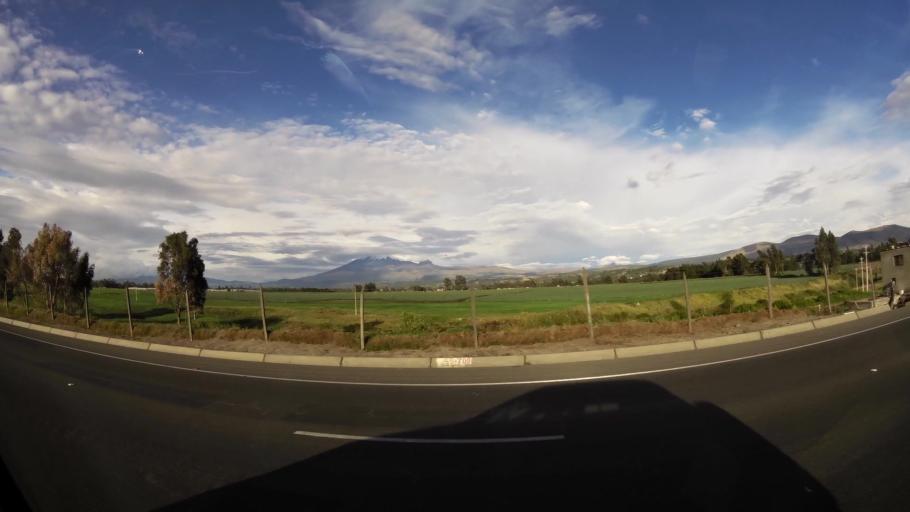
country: EC
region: Cotopaxi
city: Saquisili
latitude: -0.8282
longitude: -78.6198
